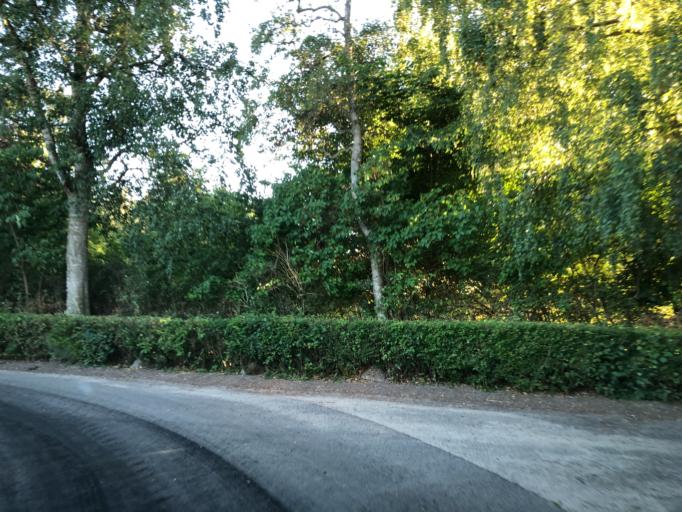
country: DK
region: Central Jutland
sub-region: Horsens Kommune
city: Horsens
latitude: 55.9321
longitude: 9.8645
